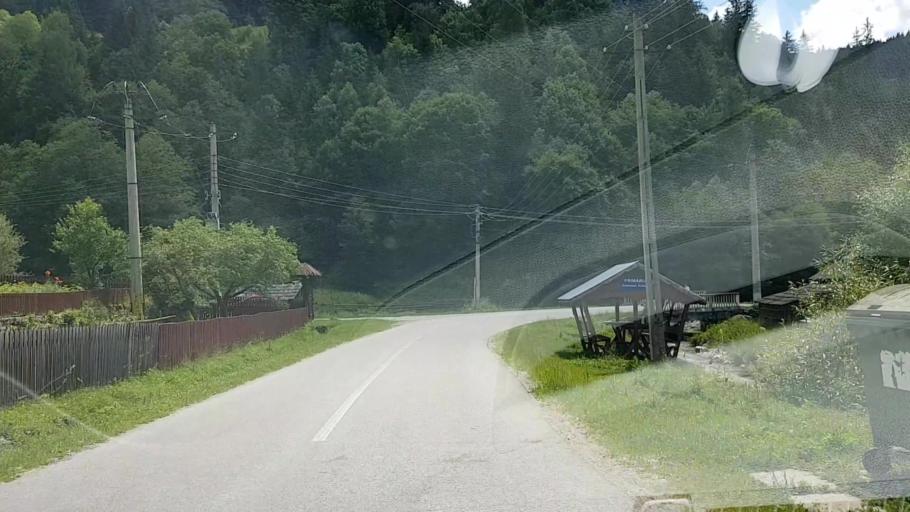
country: RO
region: Suceava
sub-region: Comuna Crucea
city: Crucea
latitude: 47.4159
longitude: 25.5848
